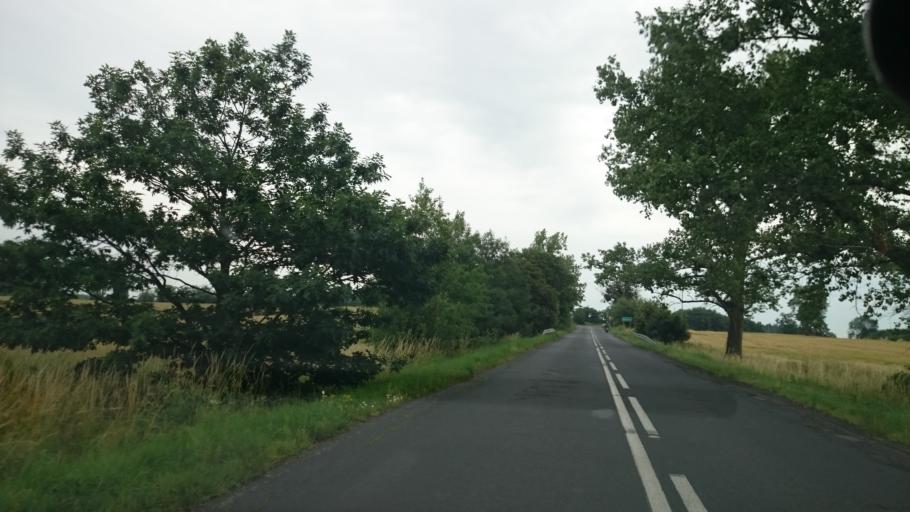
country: PL
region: Lower Silesian Voivodeship
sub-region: Powiat strzelinski
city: Przeworno
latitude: 50.6638
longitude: 17.2644
